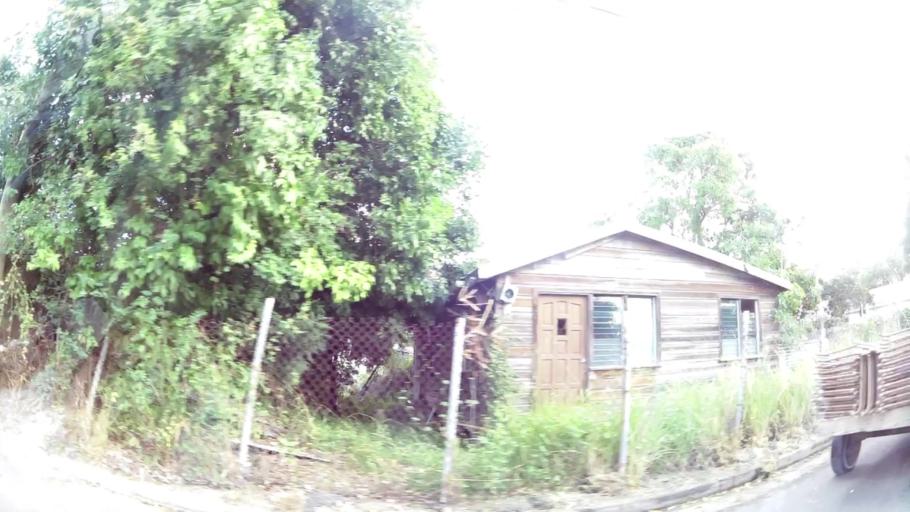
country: AG
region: Saint John
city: Saint John's
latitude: 17.1071
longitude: -61.8387
